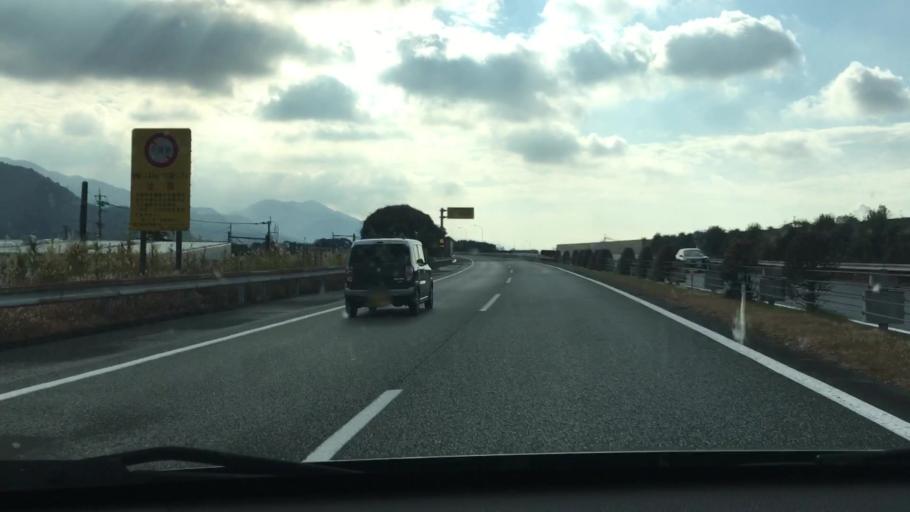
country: JP
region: Kumamoto
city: Yatsushiro
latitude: 32.5183
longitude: 130.6516
